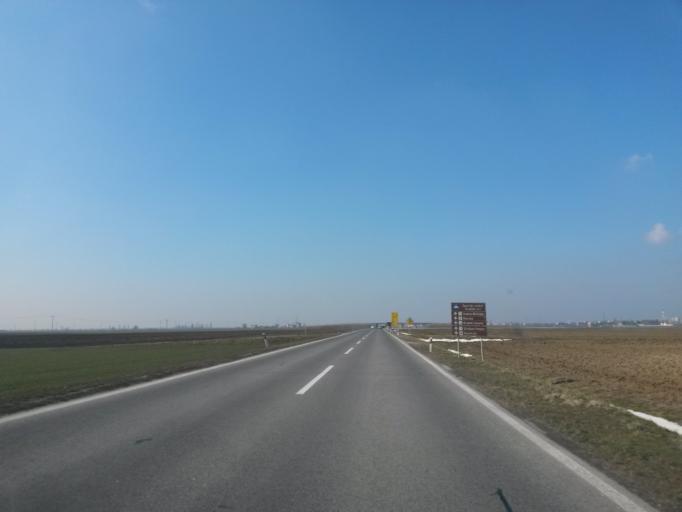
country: HR
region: Osjecko-Baranjska
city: Tenja
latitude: 45.5278
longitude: 18.7515
